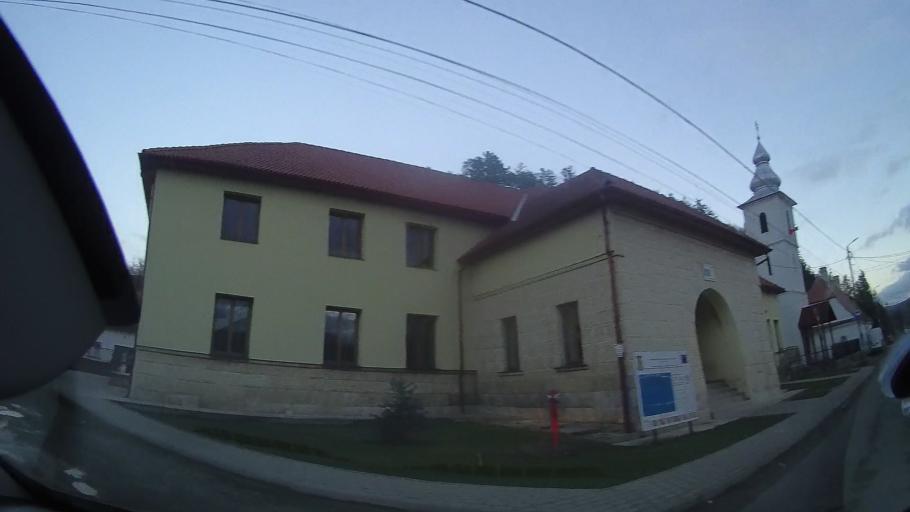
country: RO
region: Cluj
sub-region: Comuna Capusu Mare
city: Capusu Mare
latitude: 46.7915
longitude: 23.2908
